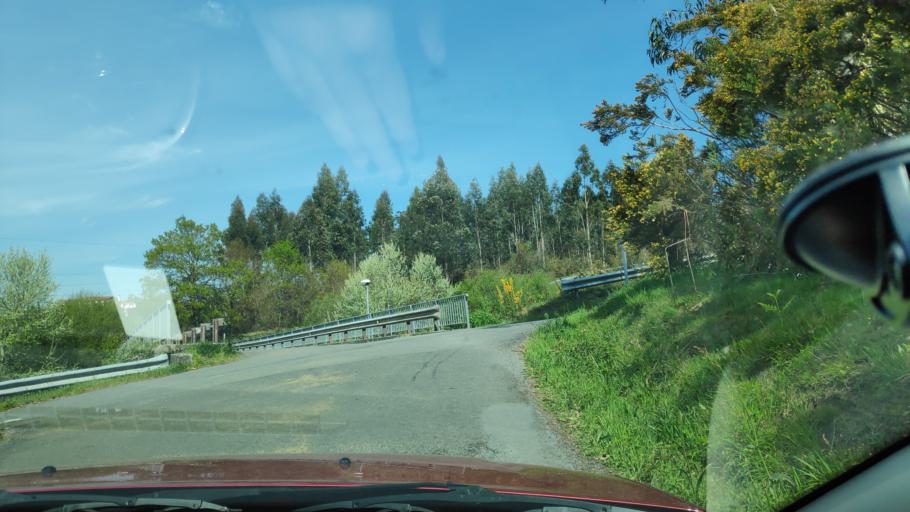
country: ES
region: Galicia
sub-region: Provincia da Coruna
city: Santiago de Compostela
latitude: 42.8966
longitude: -8.5218
